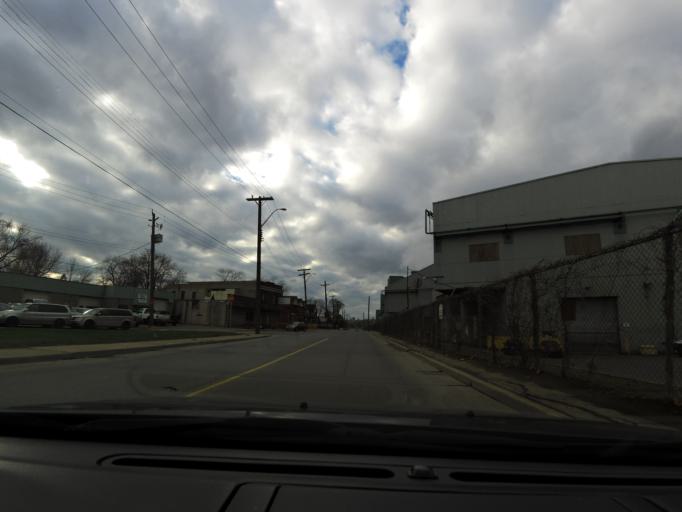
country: CA
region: Ontario
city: Hamilton
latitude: 43.2560
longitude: -79.8082
